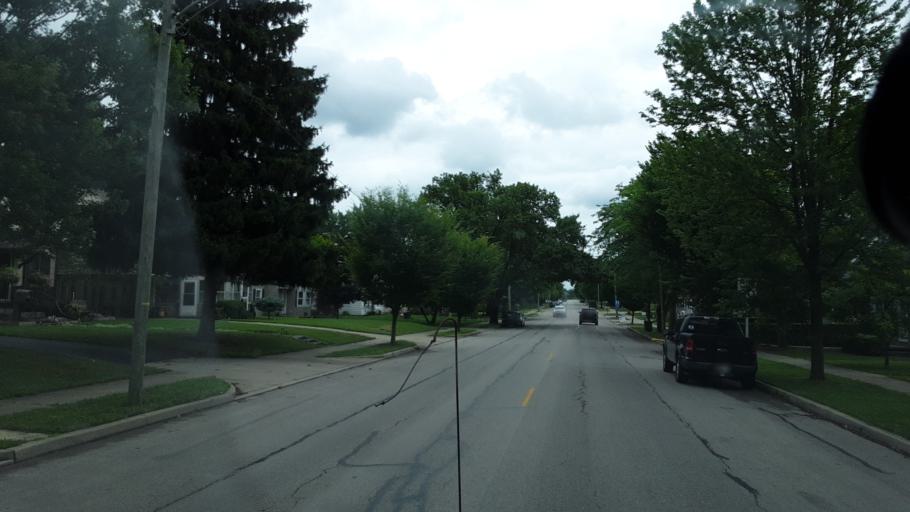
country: US
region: Indiana
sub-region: Adams County
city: Decatur
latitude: 40.8243
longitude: -84.9199
